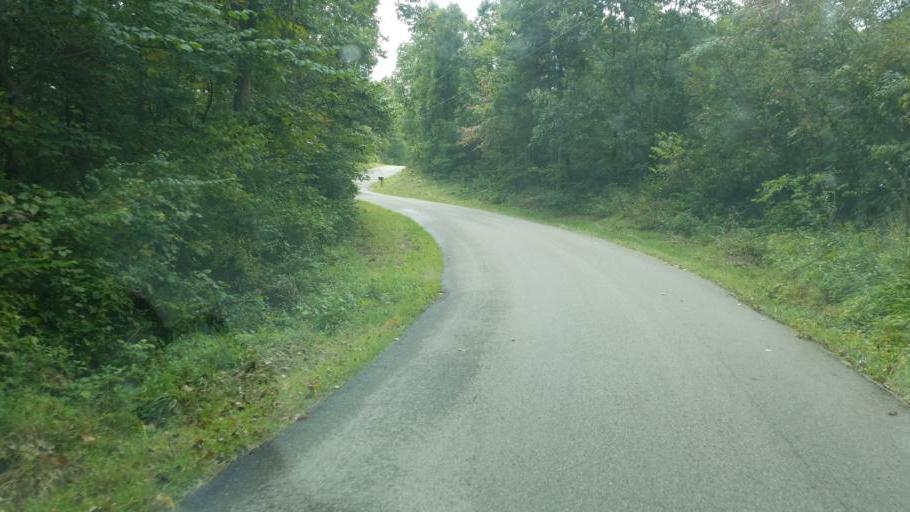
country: US
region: Ohio
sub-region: Jackson County
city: Oak Hill
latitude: 38.8996
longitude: -82.6182
